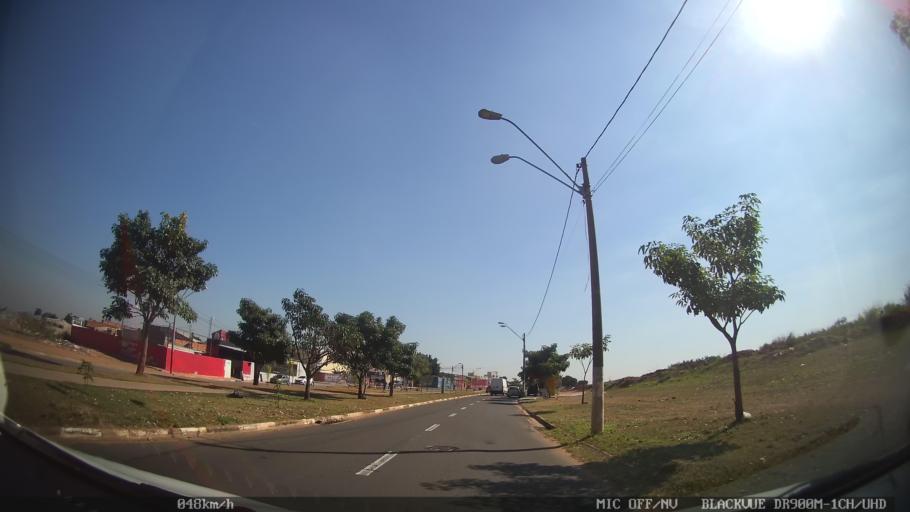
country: BR
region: Sao Paulo
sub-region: Campinas
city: Campinas
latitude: -22.9370
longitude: -47.0756
